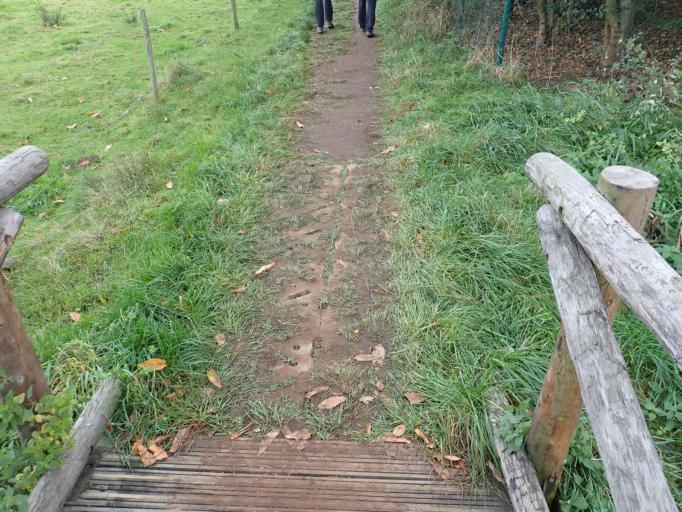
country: BE
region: Flanders
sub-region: Provincie Antwerpen
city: Duffel
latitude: 51.0790
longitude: 4.4874
